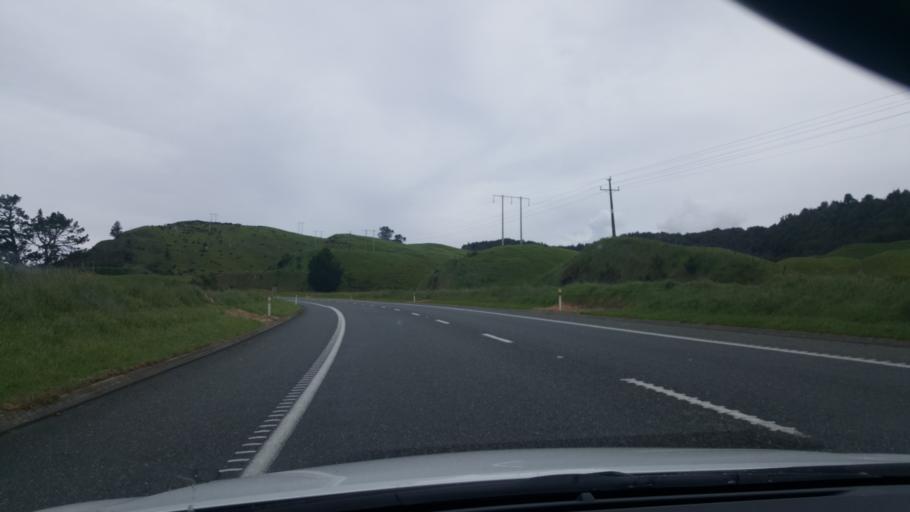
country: NZ
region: Bay of Plenty
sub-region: Rotorua District
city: Rotorua
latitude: -38.2621
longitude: 176.3205
